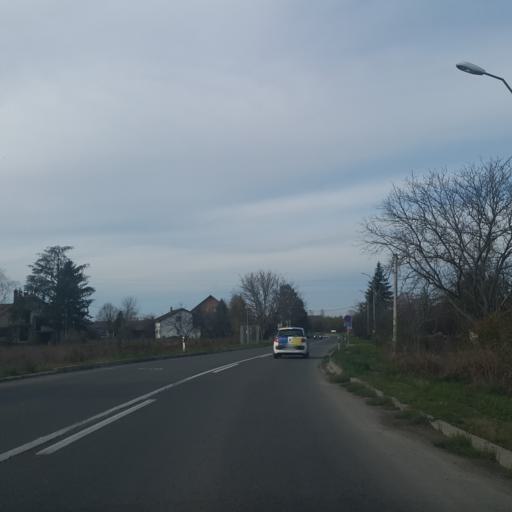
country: RS
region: Central Serbia
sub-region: Kolubarski Okrug
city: Lajkovac
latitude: 44.3681
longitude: 20.1921
